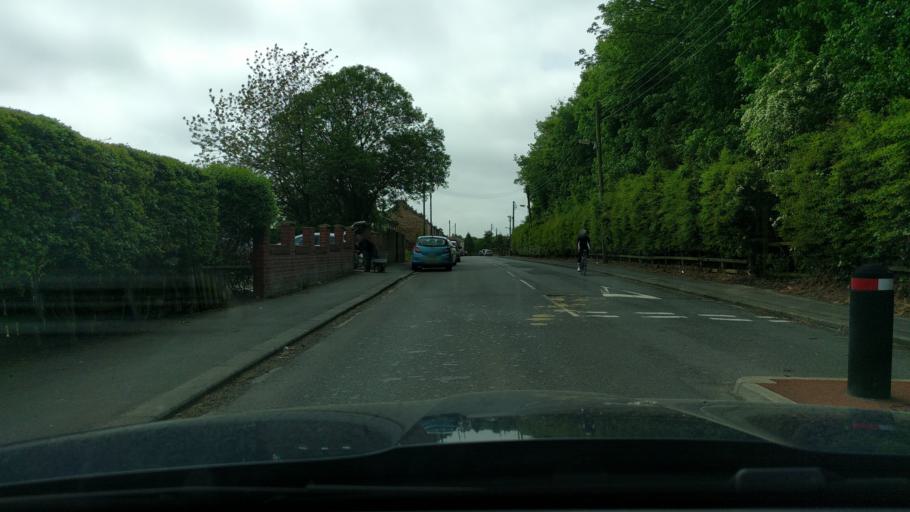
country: GB
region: England
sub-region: Northumberland
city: East Chevington
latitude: 55.2872
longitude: -1.6044
